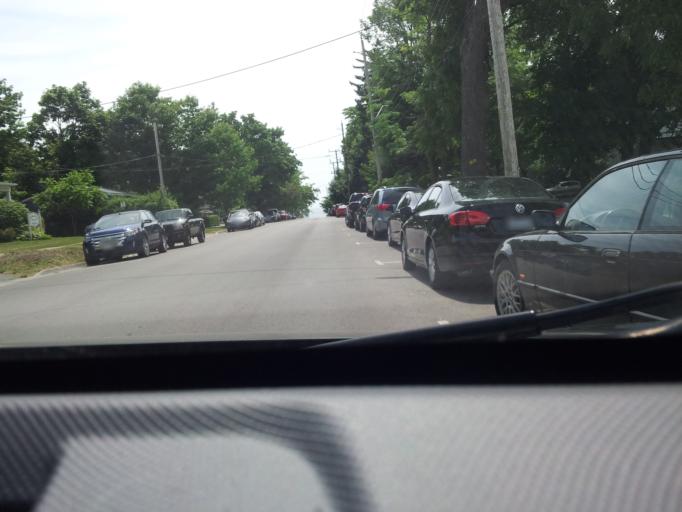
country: CA
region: Ontario
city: Norfolk County
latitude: 42.7853
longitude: -80.2038
